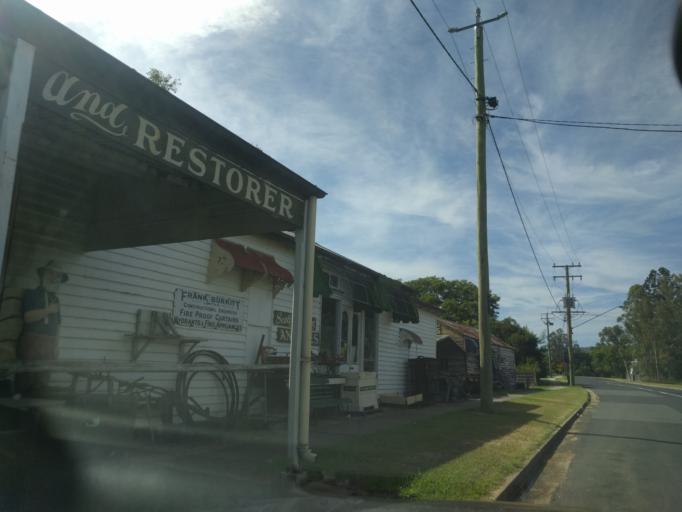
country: AU
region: Queensland
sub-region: Ipswich
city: Thagoona
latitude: -27.5664
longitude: 152.5965
